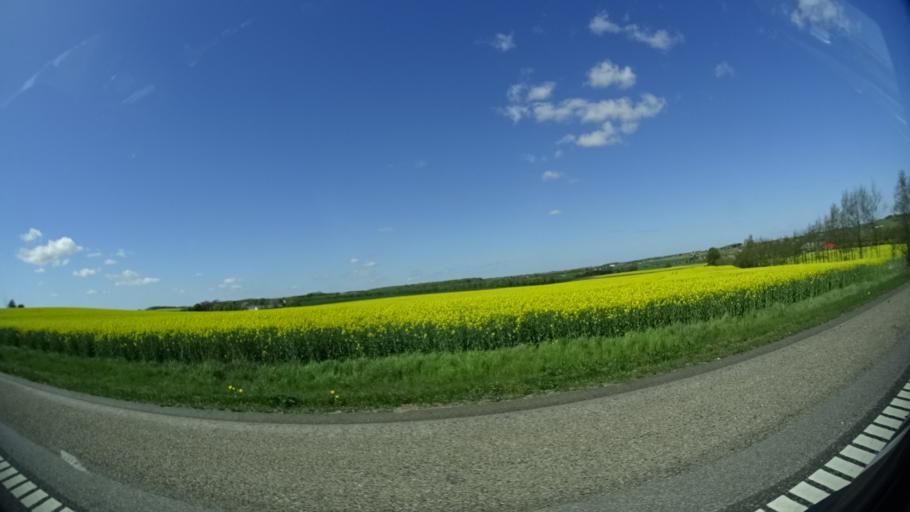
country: DK
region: Central Jutland
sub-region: Favrskov Kommune
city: Soften
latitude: 56.2133
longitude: 10.0951
